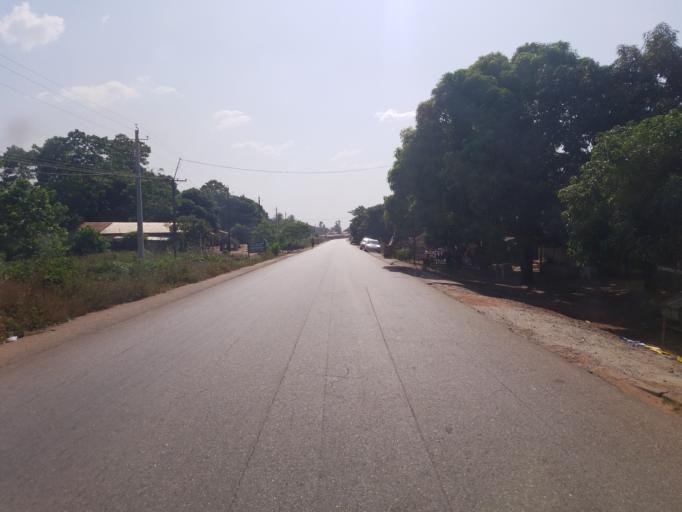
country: GN
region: Boke
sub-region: Fria
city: Fria
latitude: 10.0779
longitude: -13.7006
